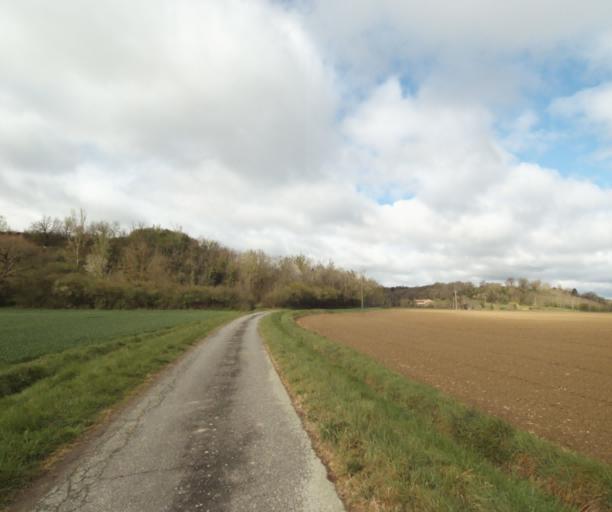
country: FR
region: Midi-Pyrenees
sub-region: Departement de l'Ariege
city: Saverdun
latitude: 43.2459
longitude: 1.5506
